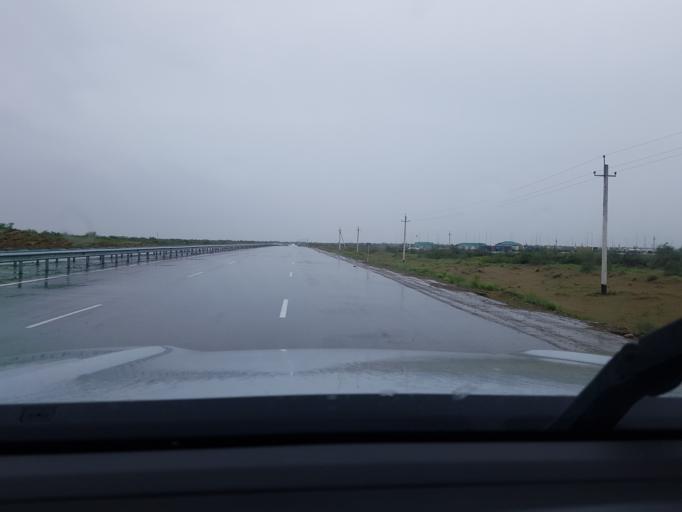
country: TM
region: Lebap
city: Farap
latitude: 39.2078
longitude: 63.6930
